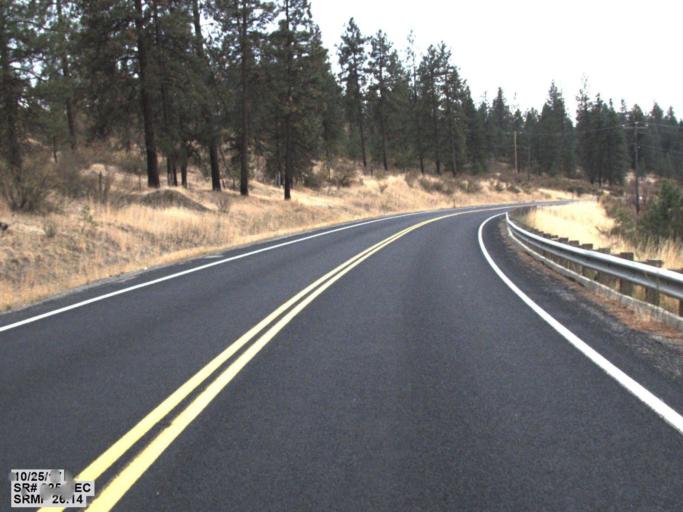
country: US
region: Washington
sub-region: Lincoln County
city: Davenport
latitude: 47.9305
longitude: -118.3211
